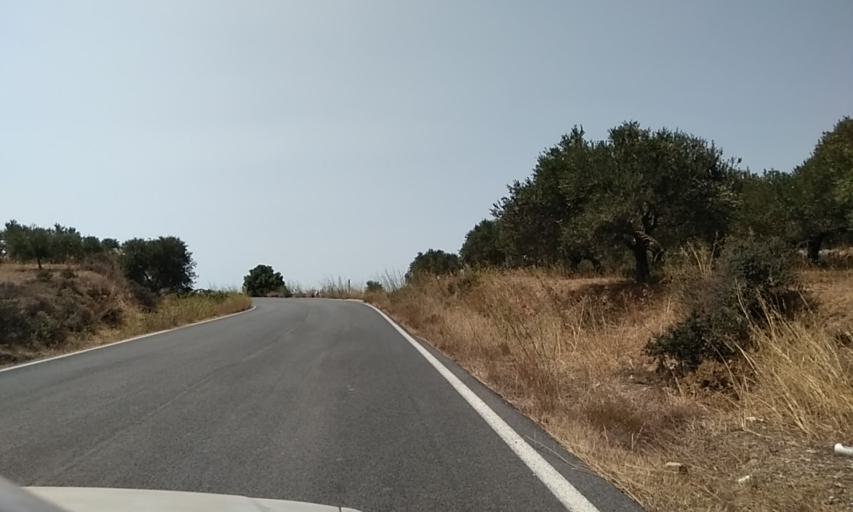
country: GR
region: Crete
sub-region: Nomos Lasithiou
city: Siteia
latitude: 35.1100
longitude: 26.0574
